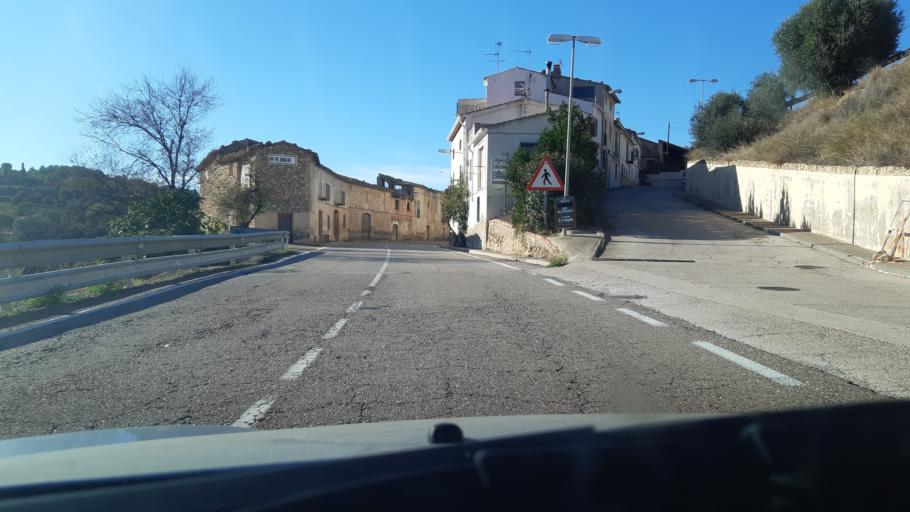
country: ES
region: Aragon
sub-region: Provincia de Teruel
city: Valjunquera
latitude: 40.9510
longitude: 0.0255
